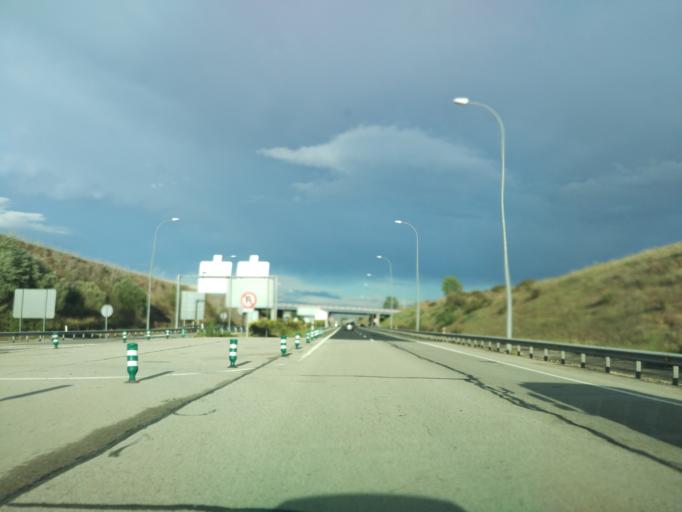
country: ES
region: Madrid
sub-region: Provincia de Madrid
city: Ajalvir
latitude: 40.5073
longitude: -3.4834
